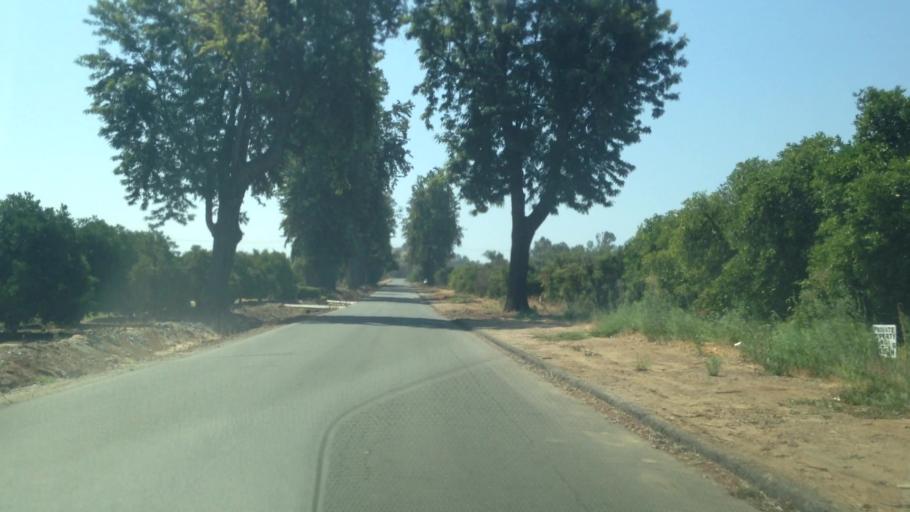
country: US
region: California
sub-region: Riverside County
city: Home Gardens
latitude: 33.8932
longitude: -117.4515
